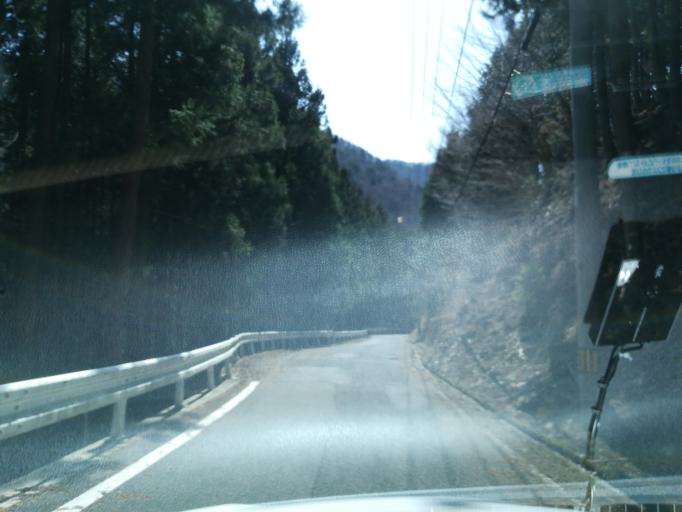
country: JP
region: Tokushima
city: Wakimachi
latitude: 33.8629
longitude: 134.0683
